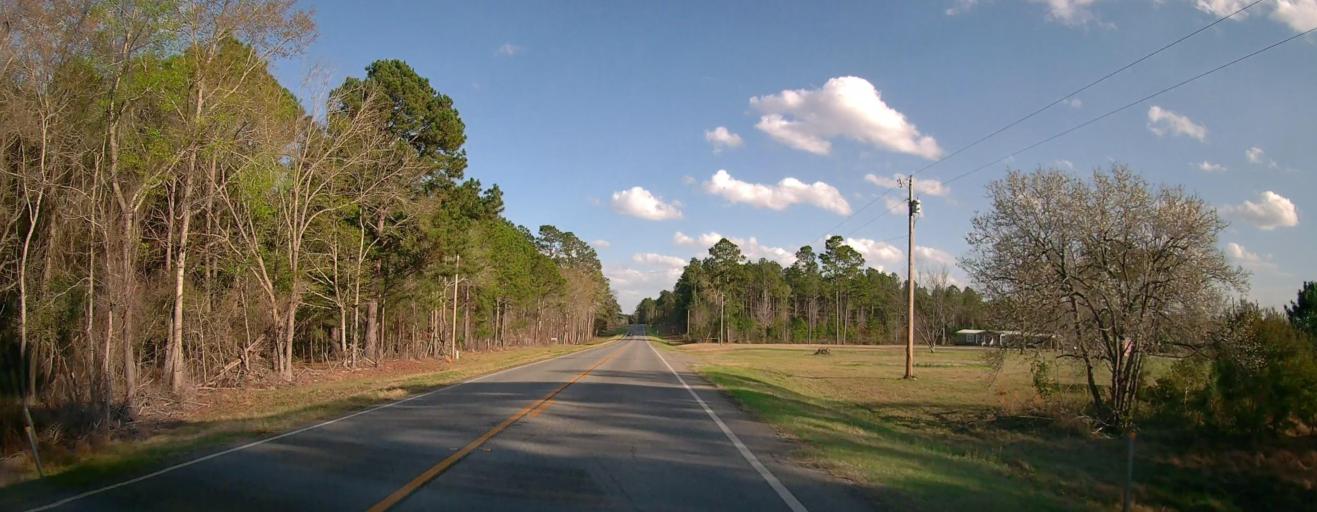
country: US
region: Georgia
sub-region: Toombs County
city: Lyons
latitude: 32.1793
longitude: -82.2896
